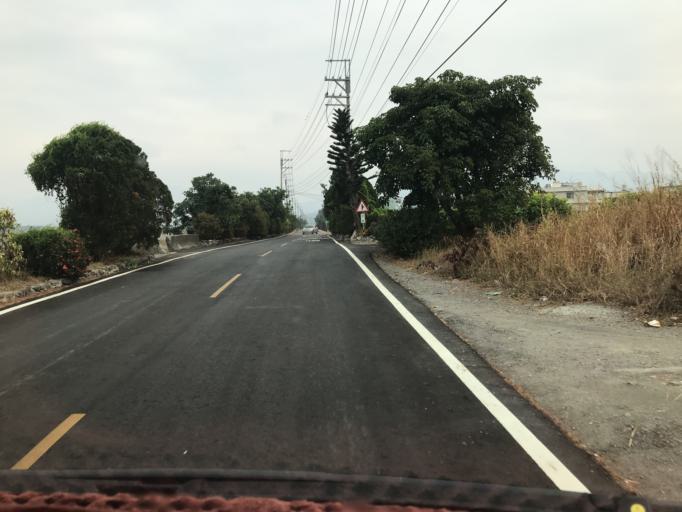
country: TW
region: Taiwan
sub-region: Pingtung
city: Pingtung
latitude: 22.4074
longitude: 120.5898
